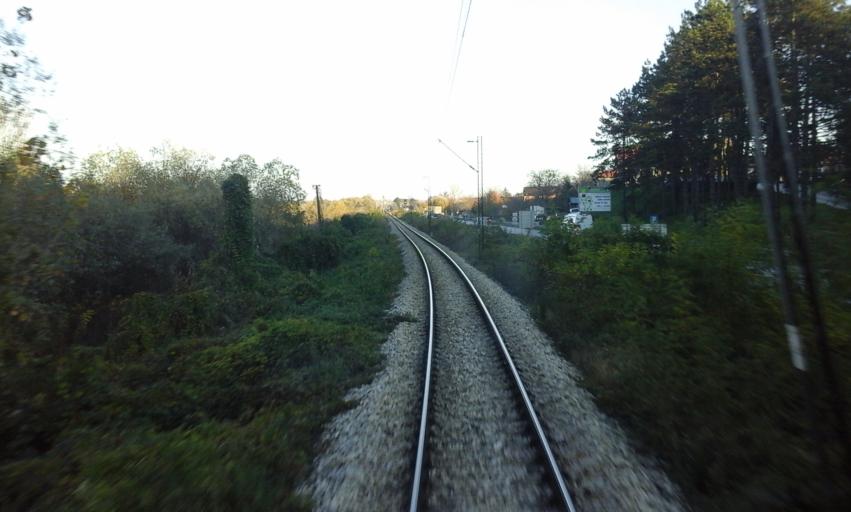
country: RS
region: Autonomna Pokrajina Vojvodina
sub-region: Juznobacki Okrug
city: Sremski Karlovci
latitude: 45.2115
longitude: 19.9185
